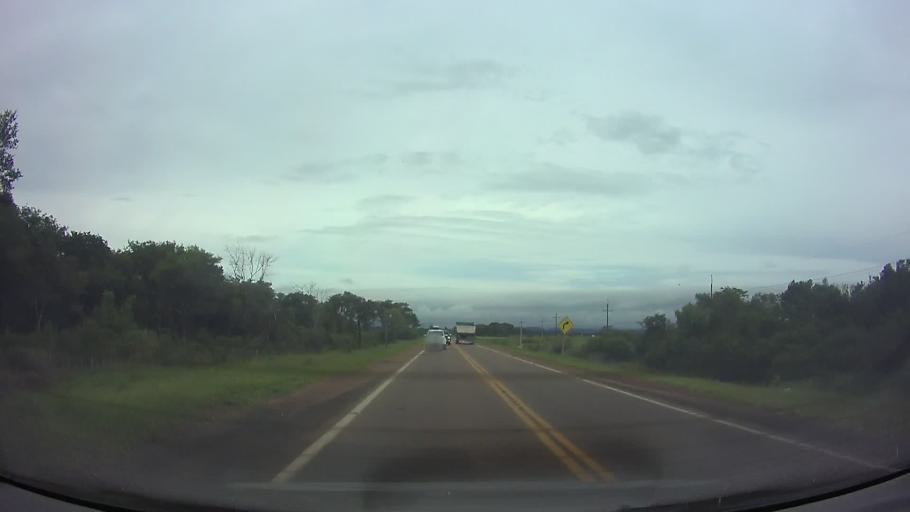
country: PY
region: Paraguari
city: Carapegua
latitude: -25.7234
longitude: -57.2041
